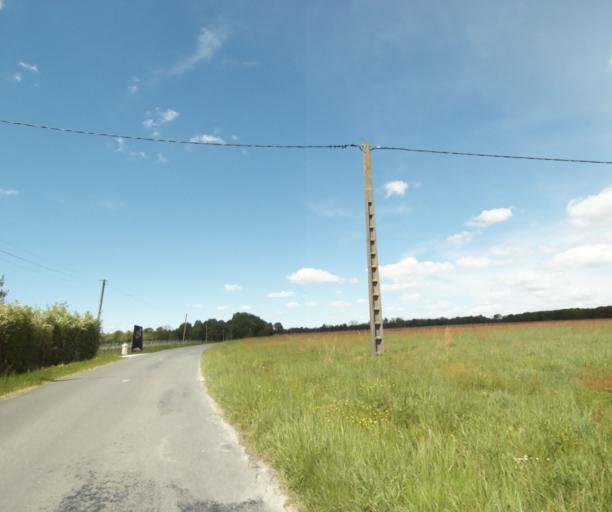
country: FR
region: Poitou-Charentes
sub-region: Departement de la Charente-Maritime
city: Burie
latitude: 45.7544
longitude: -0.4616
